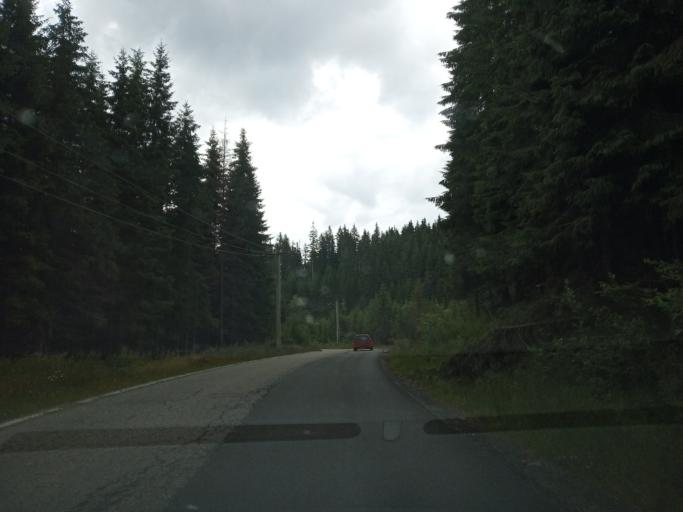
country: RO
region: Valcea
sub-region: Comuna Voineasa
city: Voineasa
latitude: 45.4163
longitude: 23.7294
